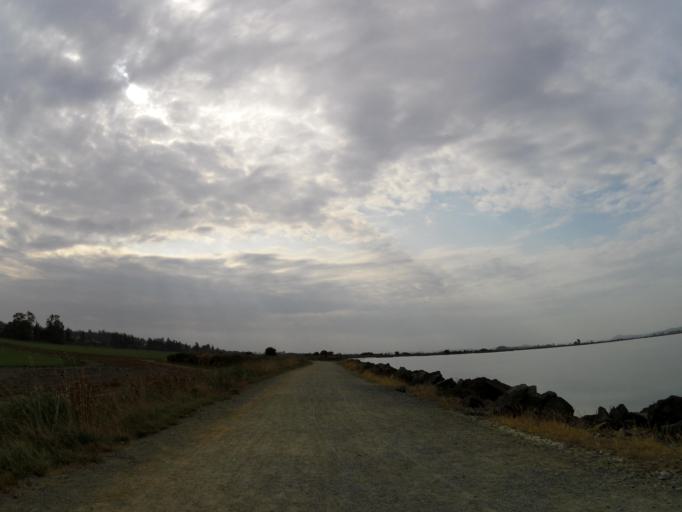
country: US
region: Washington
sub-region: Skagit County
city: Anacortes
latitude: 48.4783
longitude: -122.4716
